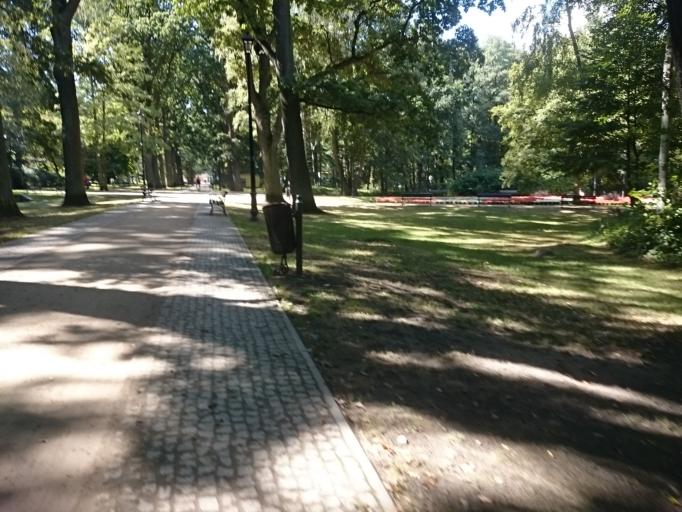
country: PL
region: West Pomeranian Voivodeship
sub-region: Swinoujscie
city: Swinoujscie
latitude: 53.9119
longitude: 14.2593
